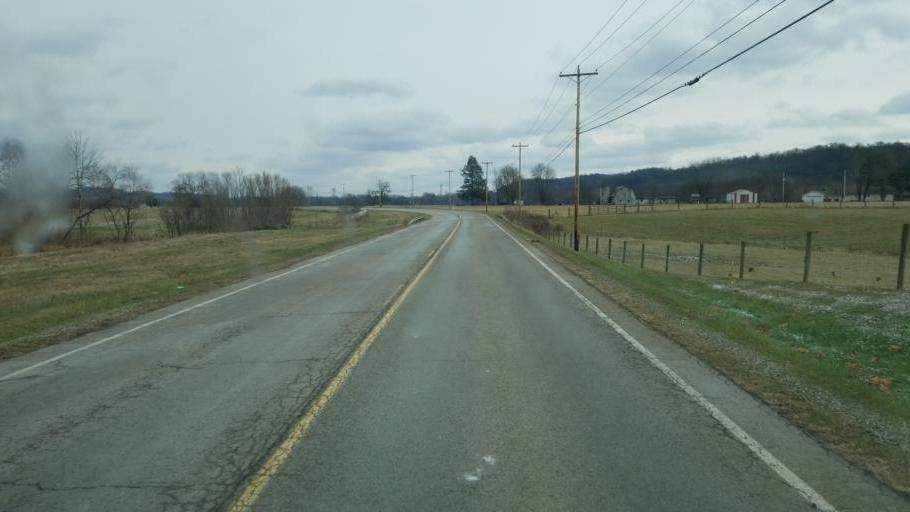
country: US
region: Ohio
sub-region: Muskingum County
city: Frazeysburg
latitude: 40.1286
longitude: -82.0899
